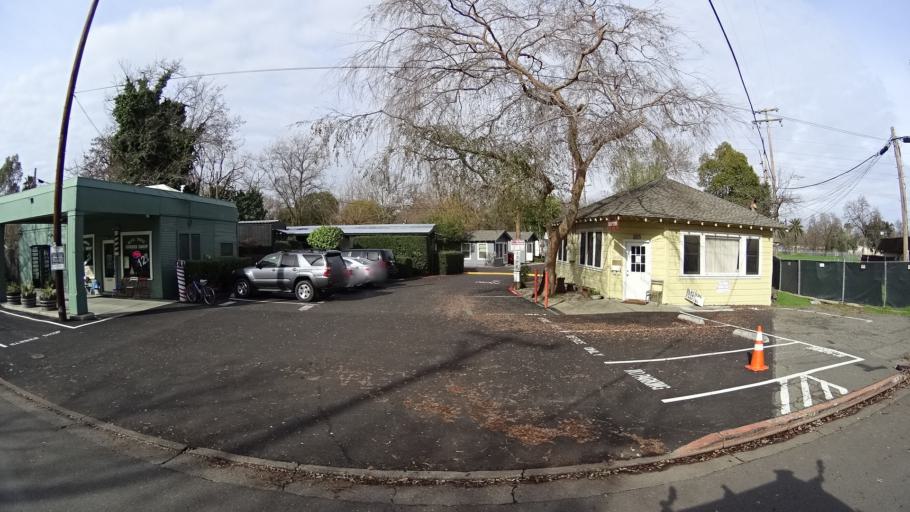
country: US
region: California
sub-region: Yolo County
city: Davis
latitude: 38.5421
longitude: -121.7367
